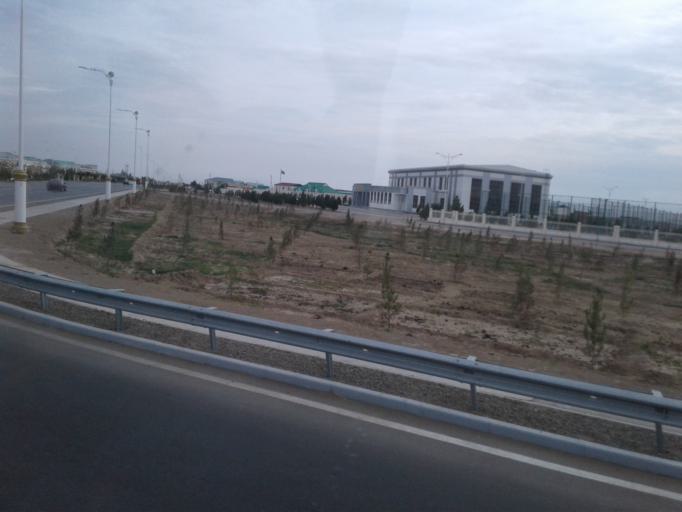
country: TM
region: Lebap
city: Turkmenabat
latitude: 38.9885
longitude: 63.5638
